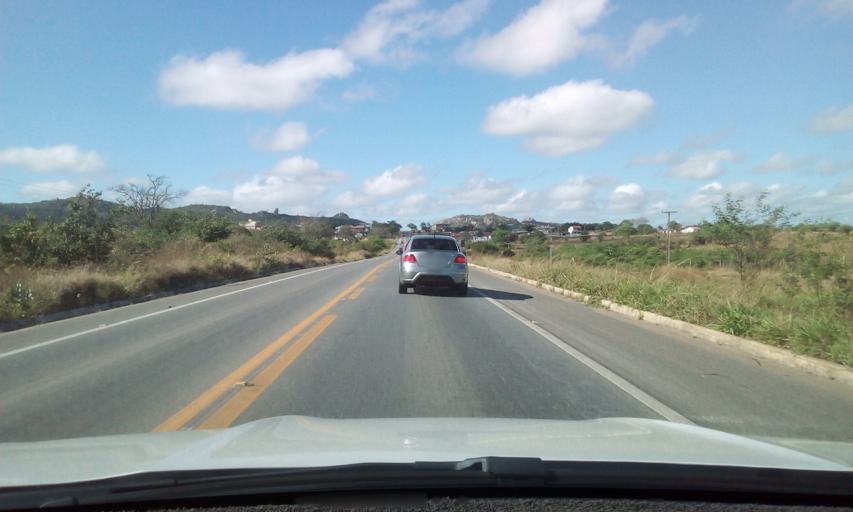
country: BR
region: Paraiba
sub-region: Campina Grande
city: Campina Grande
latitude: -7.3294
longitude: -35.8972
